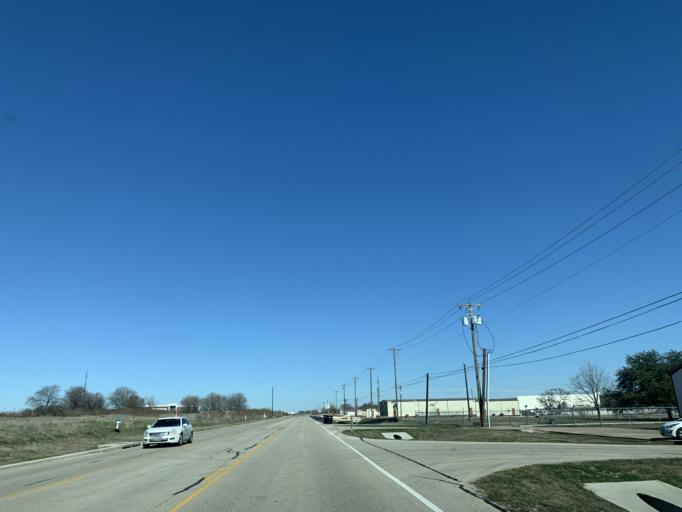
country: US
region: Texas
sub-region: Williamson County
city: Hutto
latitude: 30.5466
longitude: -97.5730
